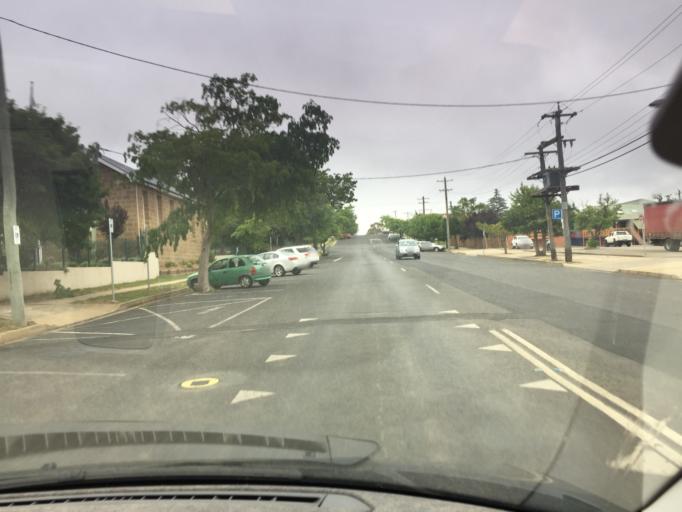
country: AU
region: New South Wales
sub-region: Cooma-Monaro
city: Cooma
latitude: -36.2367
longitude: 149.1252
